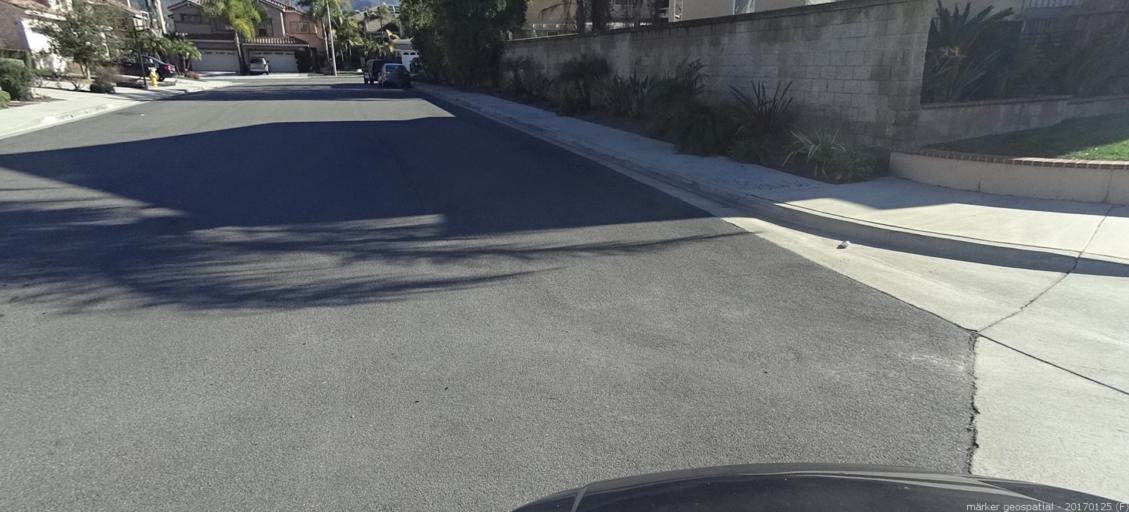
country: US
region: California
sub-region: Orange County
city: Portola Hills
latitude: 33.6771
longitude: -117.6296
